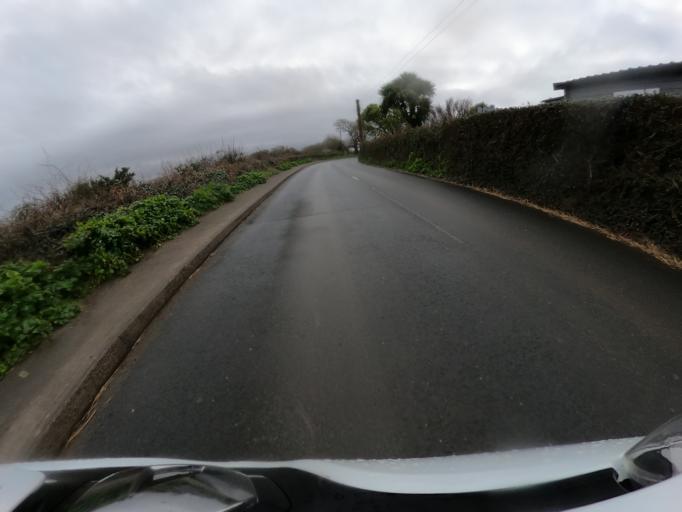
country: IM
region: Ramsey
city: Ramsey
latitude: 54.3645
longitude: -4.4505
